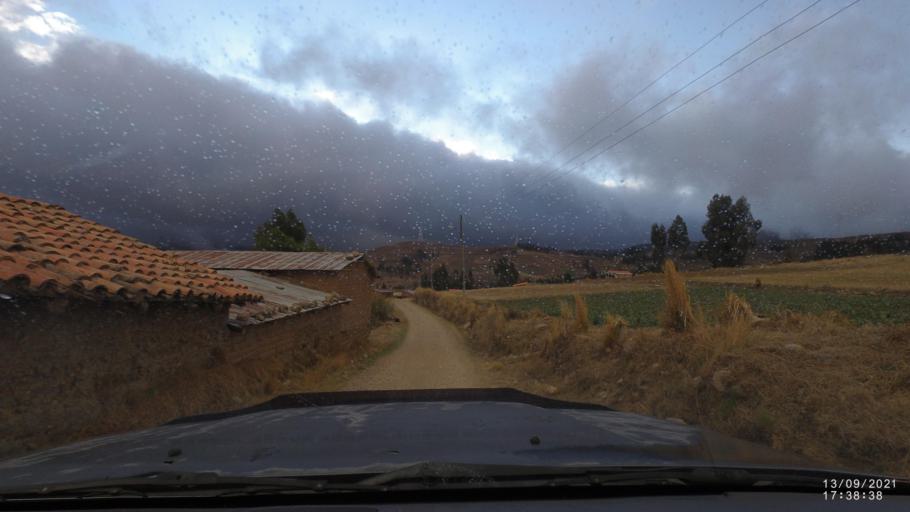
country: BO
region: Cochabamba
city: Colomi
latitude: -17.3637
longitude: -65.8065
